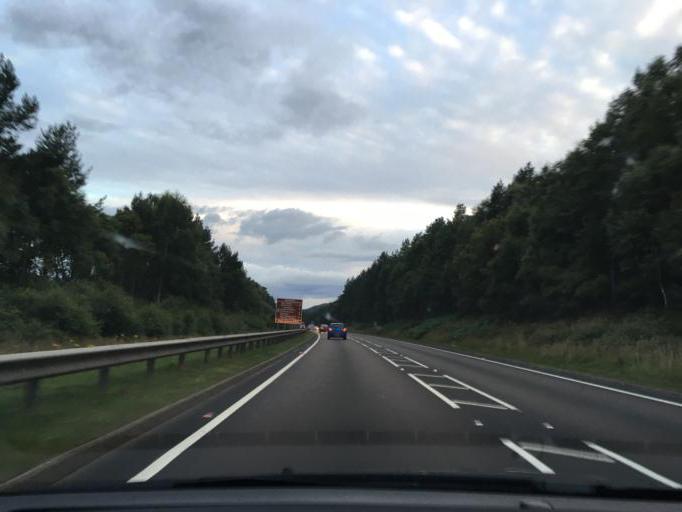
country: GB
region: Scotland
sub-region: Highland
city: Aviemore
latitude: 57.2268
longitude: -3.8187
